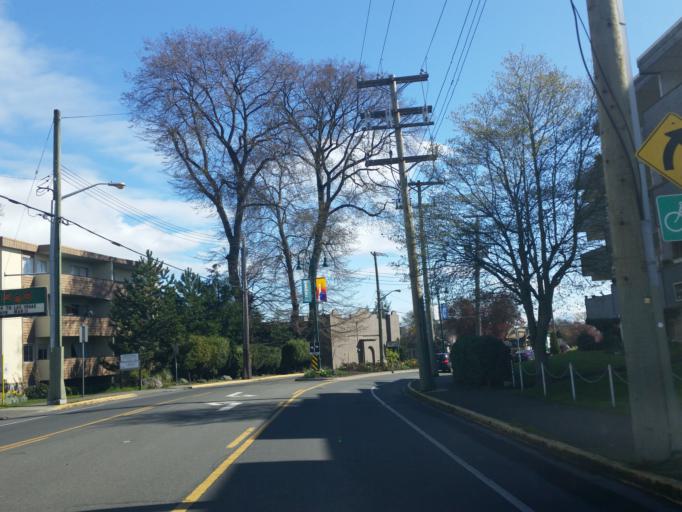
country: CA
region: British Columbia
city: Victoria
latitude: 48.4319
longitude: -123.3958
